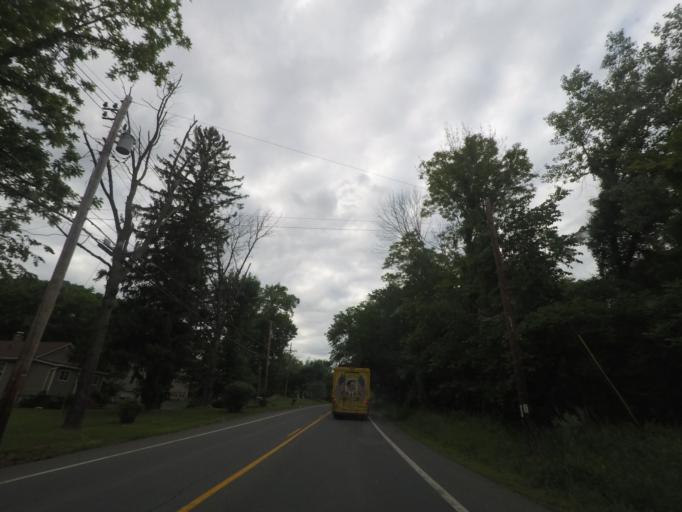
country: US
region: New York
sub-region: Orange County
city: Gardnertown
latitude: 41.5413
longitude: -74.0618
